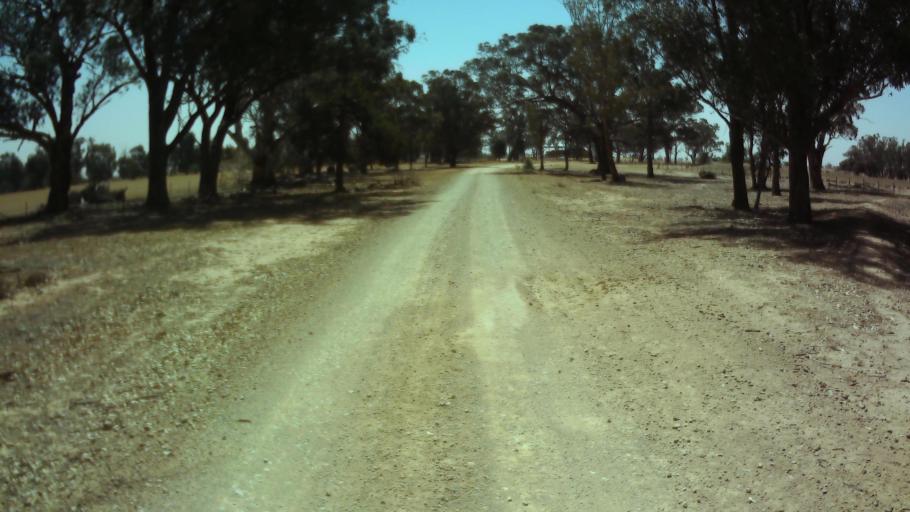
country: AU
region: New South Wales
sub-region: Weddin
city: Grenfell
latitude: -34.0166
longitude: 147.8982
